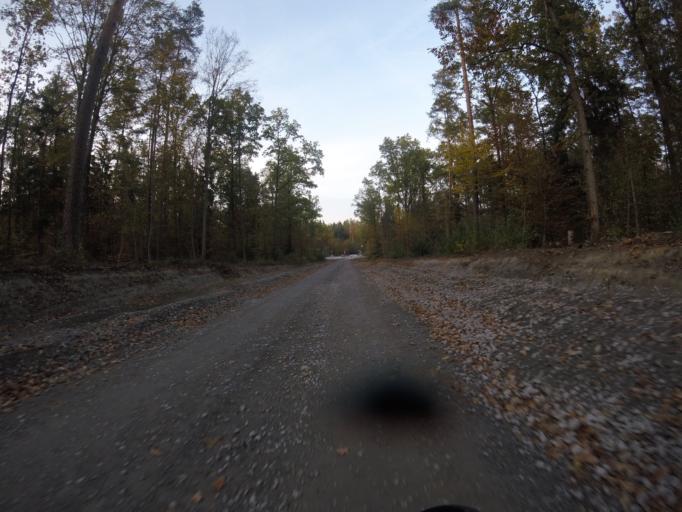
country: DE
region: Baden-Wuerttemberg
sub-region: Regierungsbezirk Stuttgart
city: Kirchberg an der Murr
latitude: 48.9827
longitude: 9.3466
